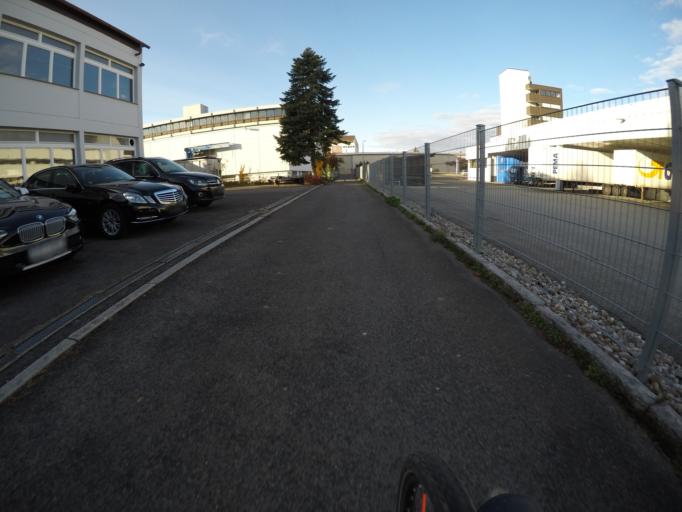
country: DE
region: Baden-Wuerttemberg
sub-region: Regierungsbezirk Stuttgart
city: Leinfelden-Echterdingen
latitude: 48.6970
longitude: 9.1465
